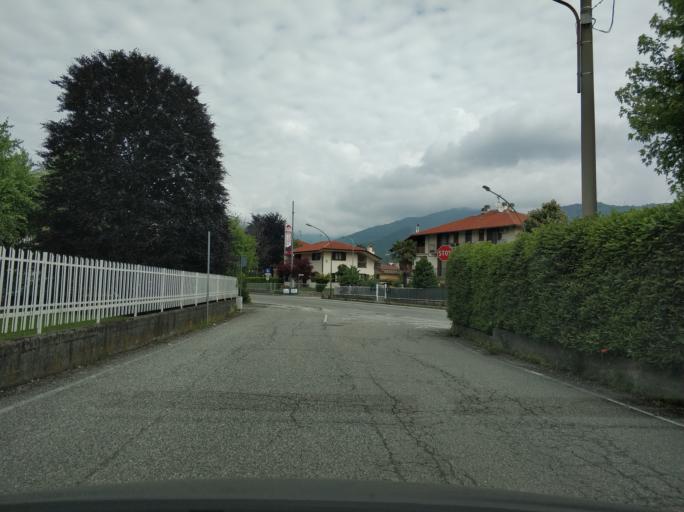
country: IT
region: Piedmont
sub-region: Provincia di Torino
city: Balangero
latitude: 45.2655
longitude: 7.5216
